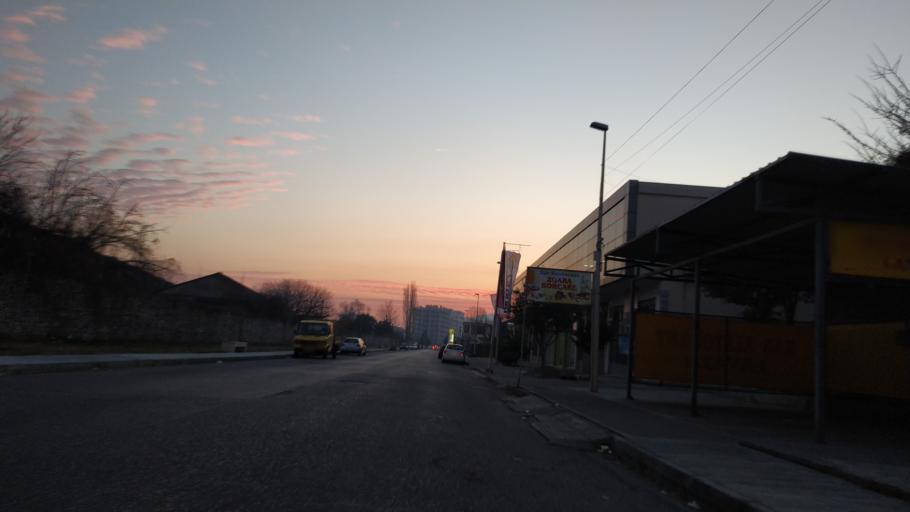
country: AL
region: Shkoder
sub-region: Rrethi i Shkodres
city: Shkoder
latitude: 42.0812
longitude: 19.5253
